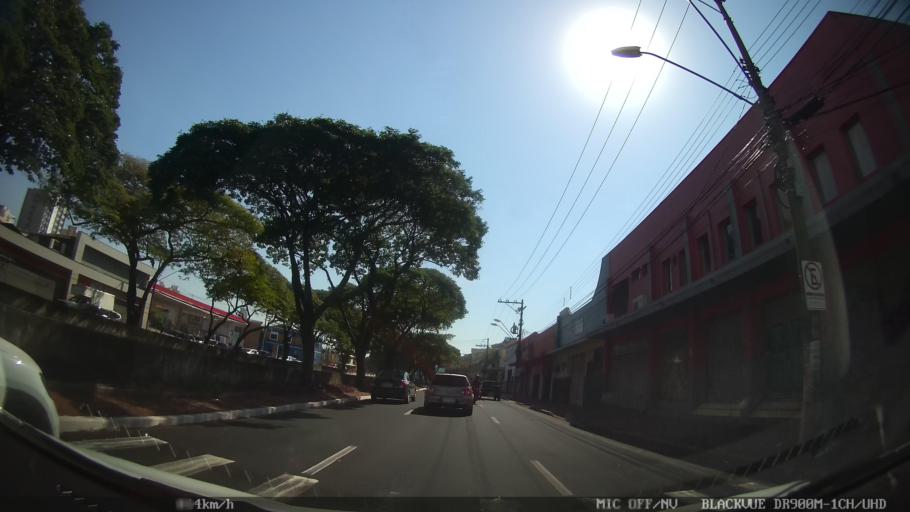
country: BR
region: Sao Paulo
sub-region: Ribeirao Preto
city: Ribeirao Preto
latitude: -21.1790
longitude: -47.8008
